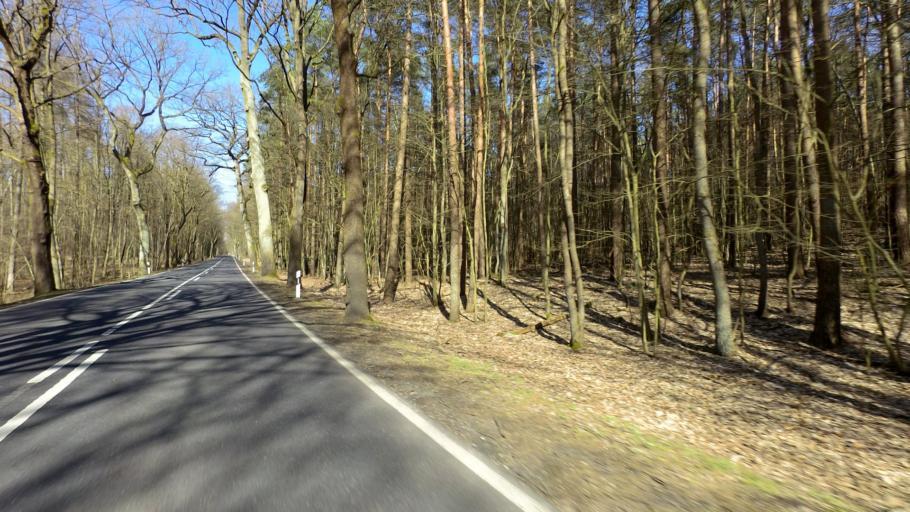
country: DE
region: Brandenburg
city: Werftpfuhl
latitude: 52.6692
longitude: 13.8290
